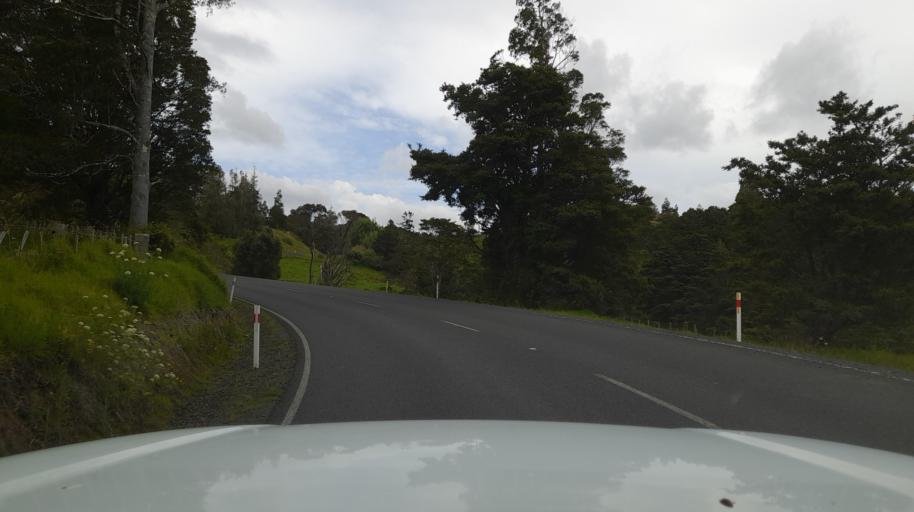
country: NZ
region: Northland
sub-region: Far North District
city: Kaitaia
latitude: -35.3047
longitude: 173.3458
